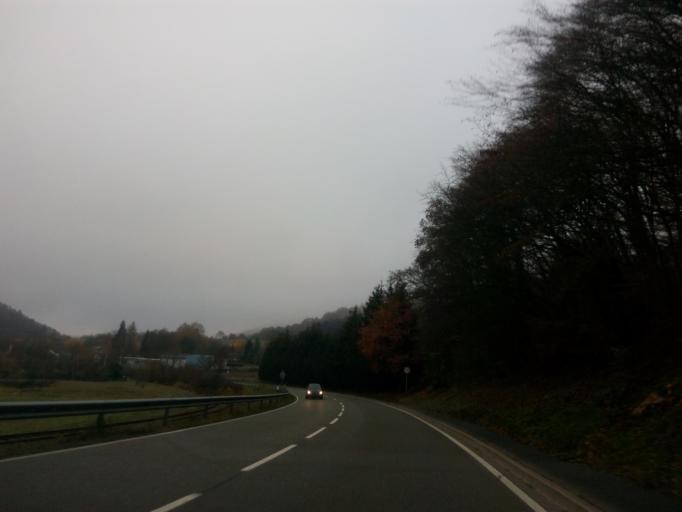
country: DE
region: Rheinland-Pfalz
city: Oberweiler-Tiefenbach
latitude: 49.5984
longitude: 7.6057
